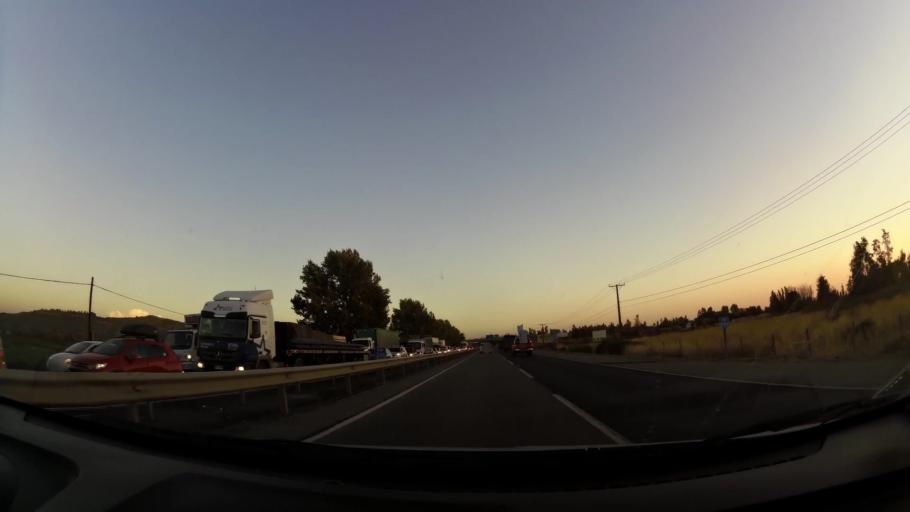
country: CL
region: Maule
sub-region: Provincia de Linares
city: Linares
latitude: -35.7572
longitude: -71.6721
